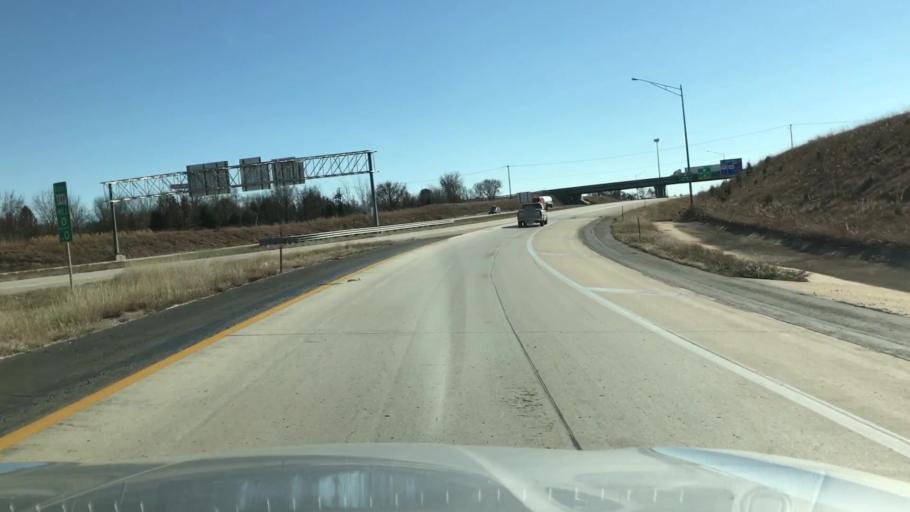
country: US
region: Missouri
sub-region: Jasper County
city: Duenweg
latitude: 37.0576
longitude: -94.4270
